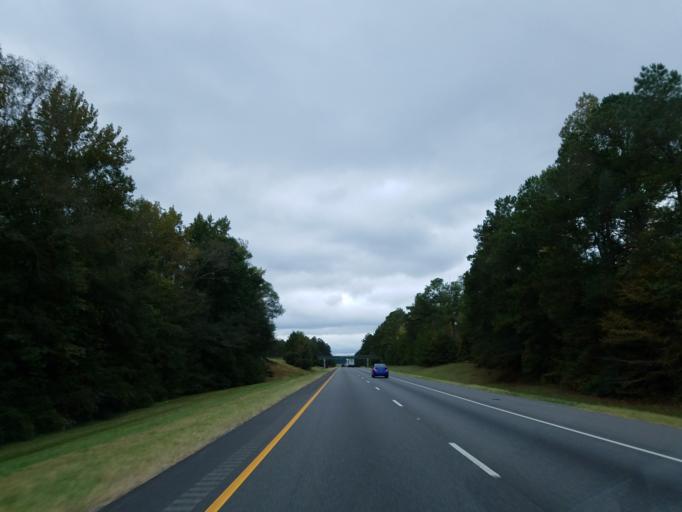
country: US
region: Alabama
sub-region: Hale County
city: Moundville
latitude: 33.0075
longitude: -87.7622
